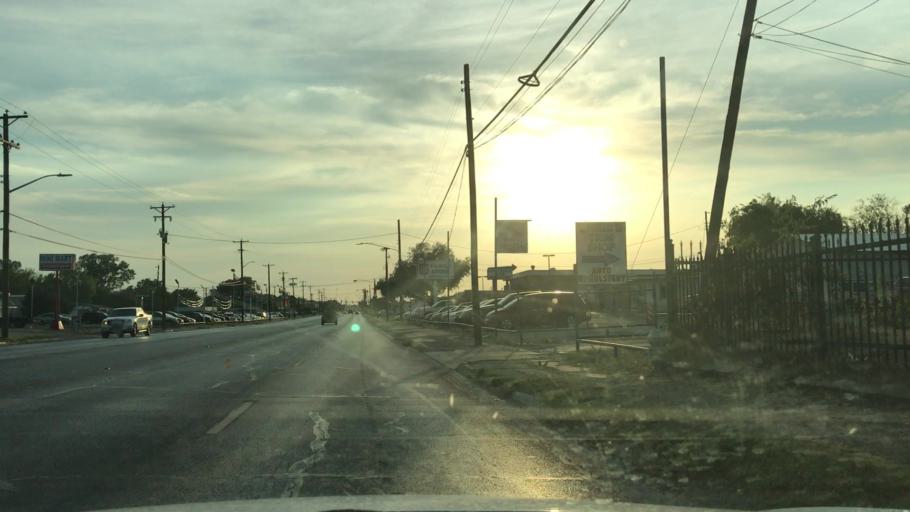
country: US
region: Texas
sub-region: Tarrant County
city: Haltom City
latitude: 32.7952
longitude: -97.3031
